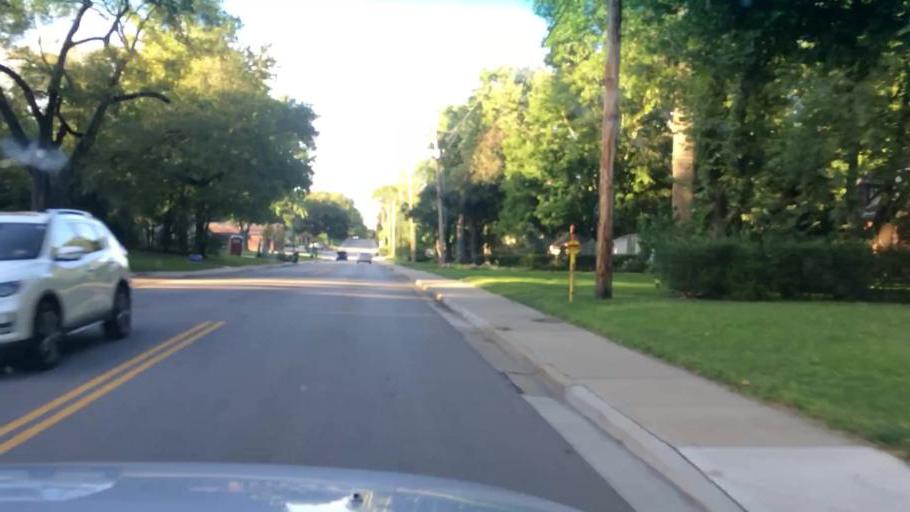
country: US
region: Kansas
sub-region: Johnson County
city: Fairway
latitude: 39.0182
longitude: -94.6303
